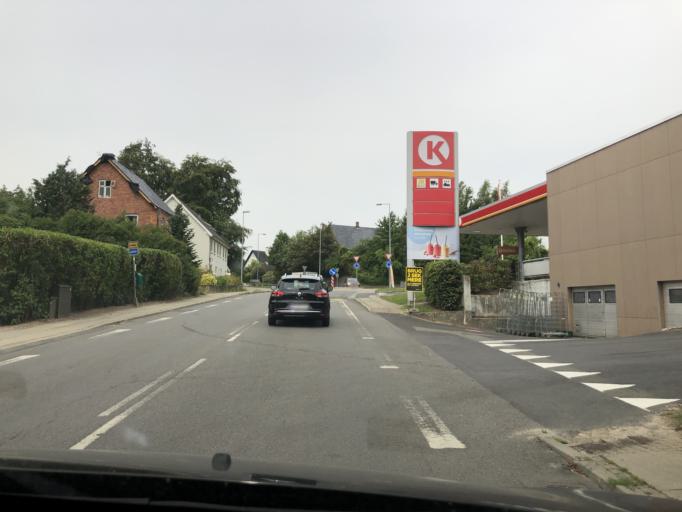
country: DK
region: South Denmark
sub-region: Assens Kommune
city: Glamsbjerg
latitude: 55.2696
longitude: 10.1132
